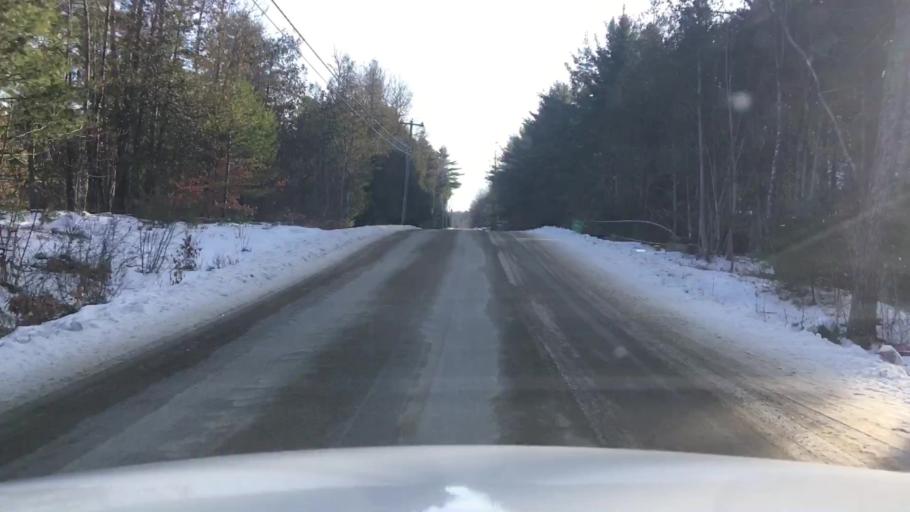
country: US
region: Maine
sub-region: Penobscot County
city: Holden
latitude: 44.7729
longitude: -68.5845
